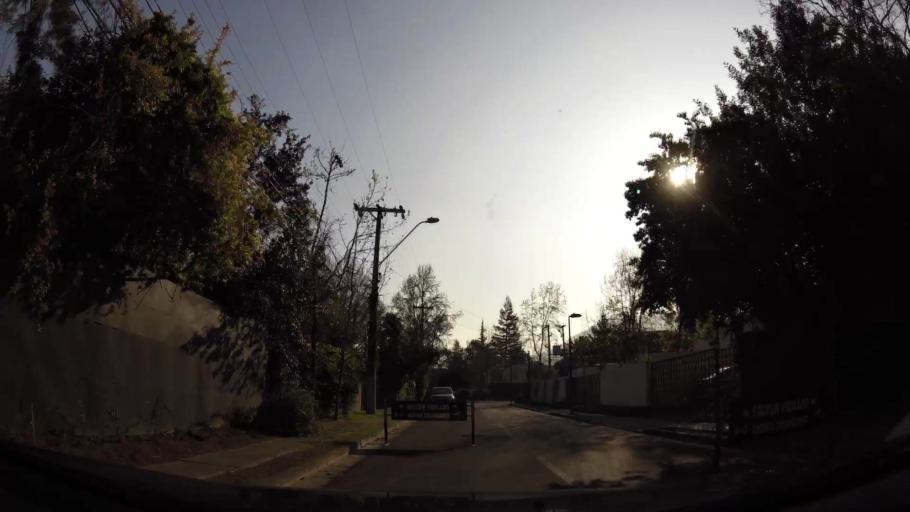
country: CL
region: Santiago Metropolitan
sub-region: Provincia de Santiago
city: Villa Presidente Frei, Nunoa, Santiago, Chile
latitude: -33.3624
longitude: -70.5335
